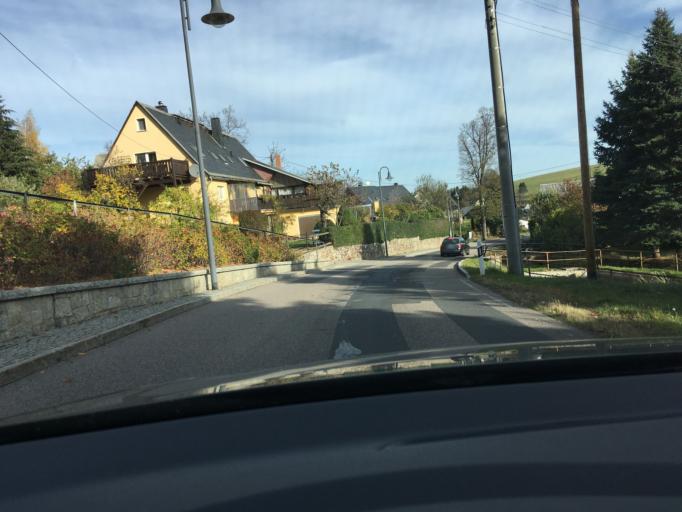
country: DE
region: Saxony
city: Barenstein
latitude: 50.8302
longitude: 13.8047
